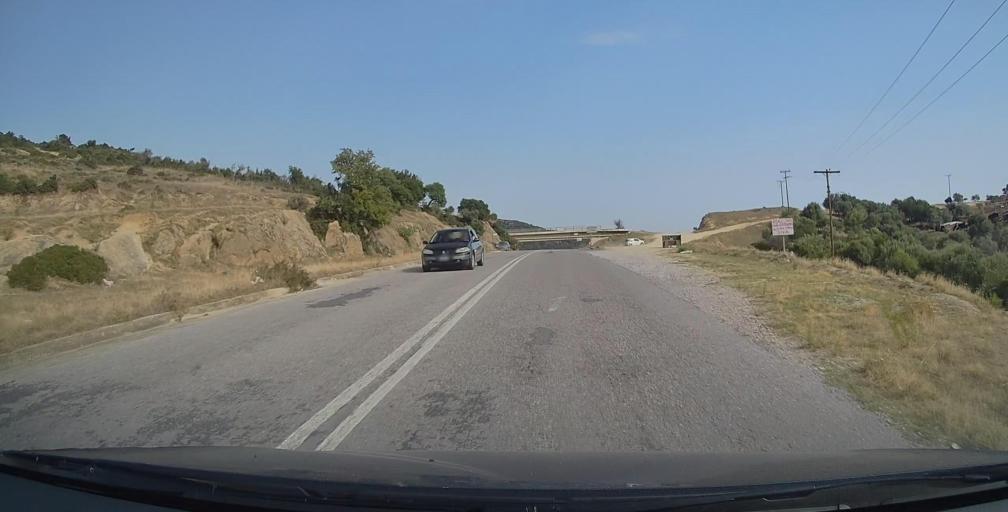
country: GR
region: Central Macedonia
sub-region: Nomos Chalkidikis
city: Sykia
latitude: 40.0175
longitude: 23.9867
